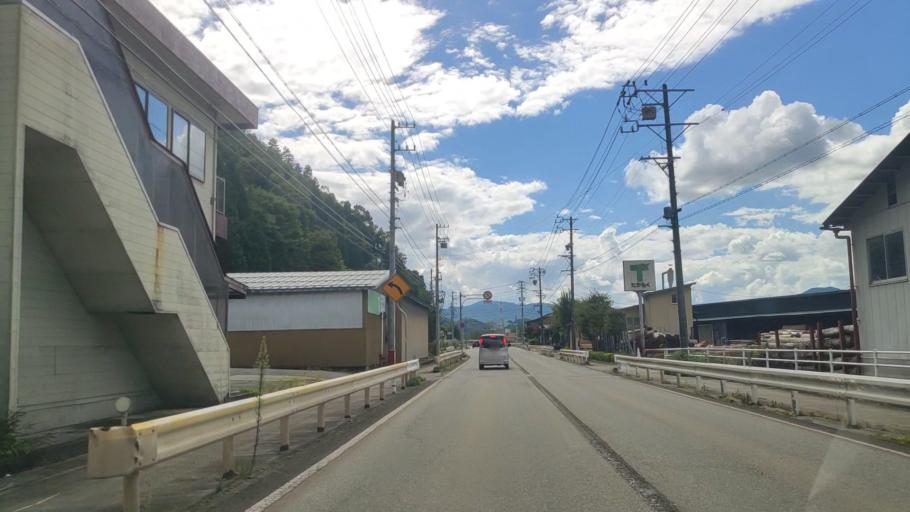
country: JP
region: Gifu
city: Takayama
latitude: 36.1811
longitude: 137.2510
